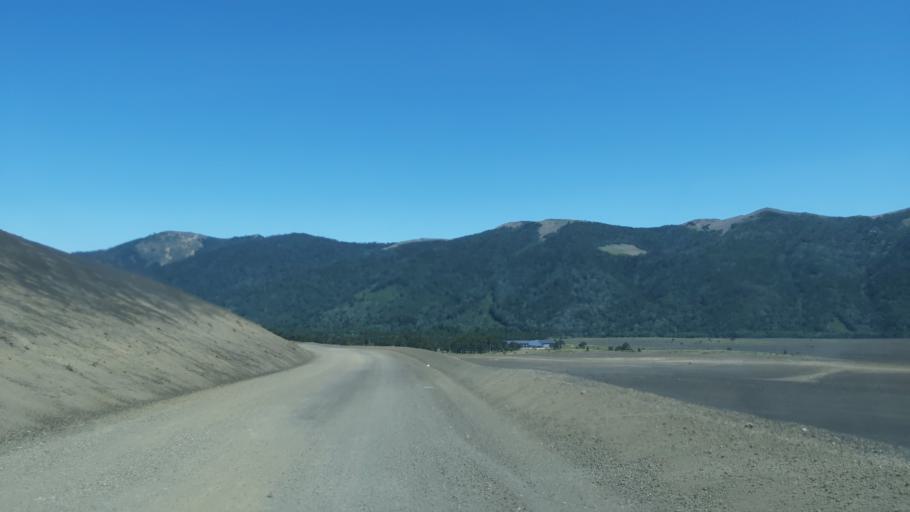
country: CL
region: Araucania
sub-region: Provincia de Cautin
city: Vilcun
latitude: -38.4092
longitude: -71.5424
